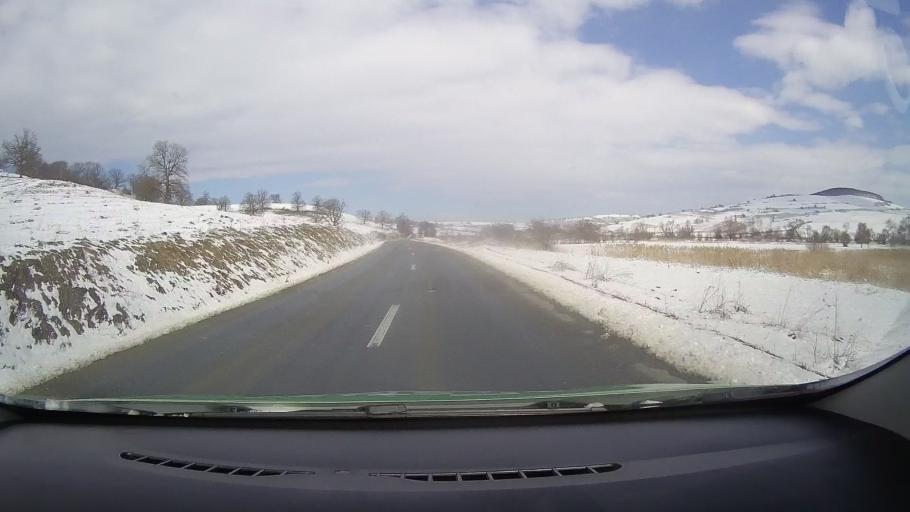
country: RO
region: Sibiu
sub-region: Comuna Altina
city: Altina
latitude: 45.9489
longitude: 24.4512
